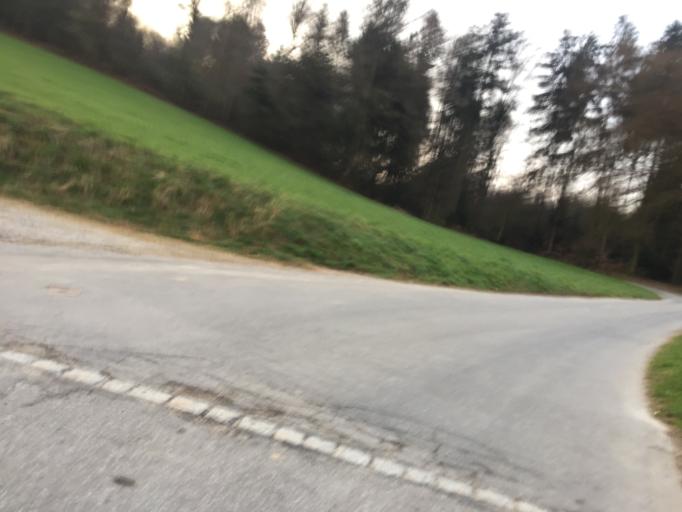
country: CH
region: Bern
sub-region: Bern-Mittelland District
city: Koniz
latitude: 46.9199
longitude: 7.4261
